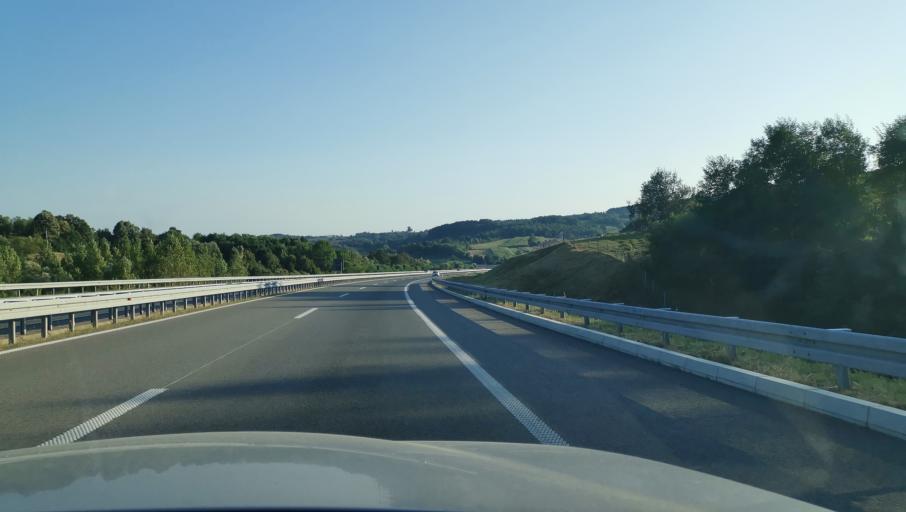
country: RS
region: Central Serbia
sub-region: Moravicki Okrug
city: Gornji Milanovac
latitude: 44.0920
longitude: 20.3782
